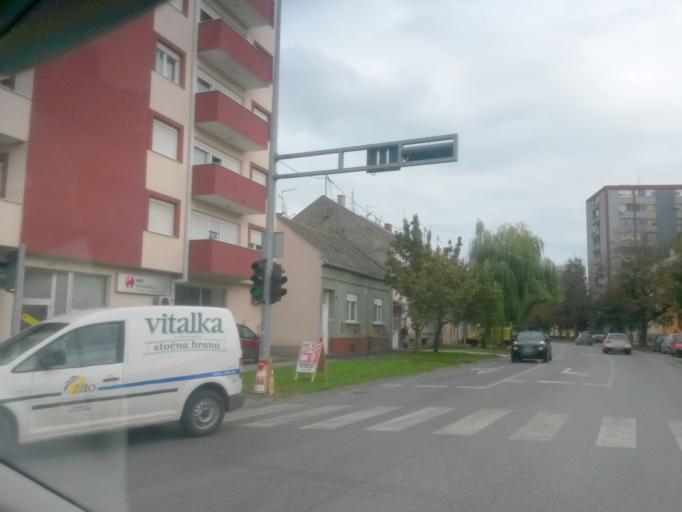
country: HR
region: Osjecko-Baranjska
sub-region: Grad Osijek
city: Osijek
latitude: 45.5562
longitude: 18.6694
